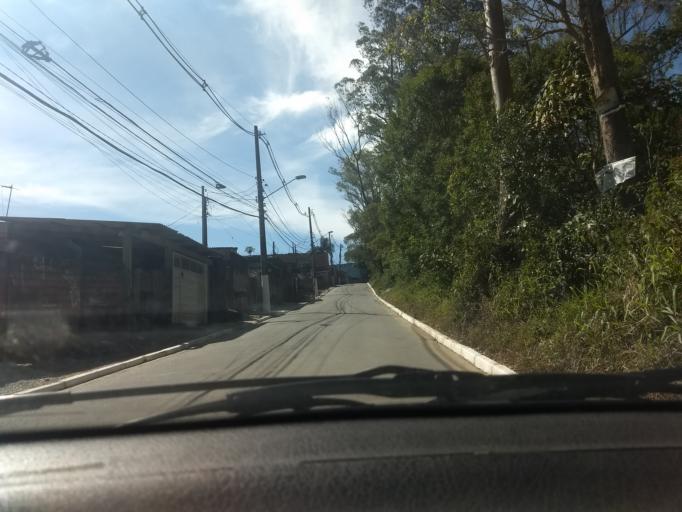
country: BR
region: Sao Paulo
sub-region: Embu-Guacu
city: Embu Guacu
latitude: -23.8260
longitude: -46.7105
